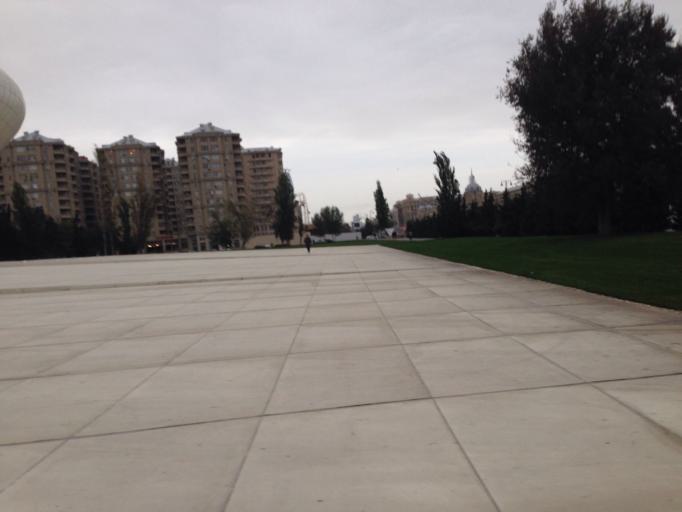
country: AZ
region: Baki
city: Baku
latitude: 40.3952
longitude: 49.8684
